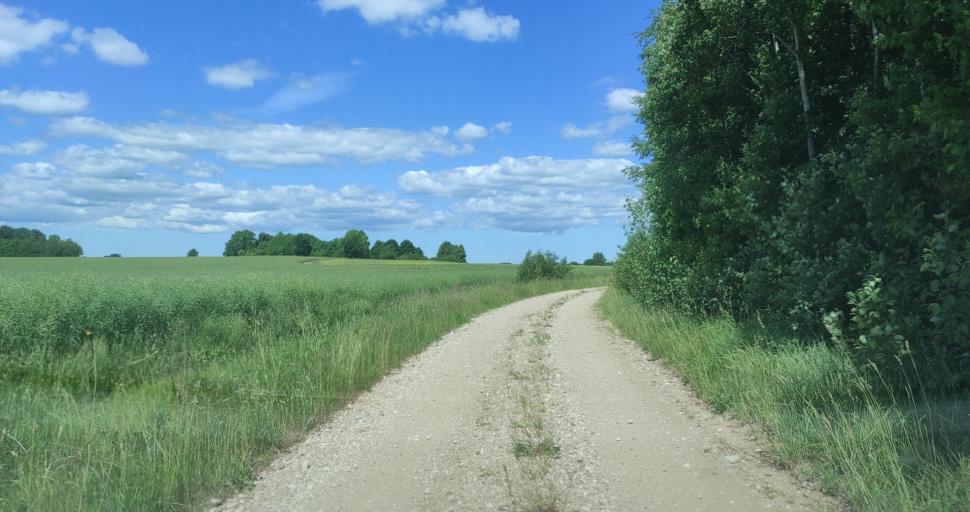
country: LV
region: Aizpute
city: Aizpute
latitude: 56.8564
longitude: 21.7137
